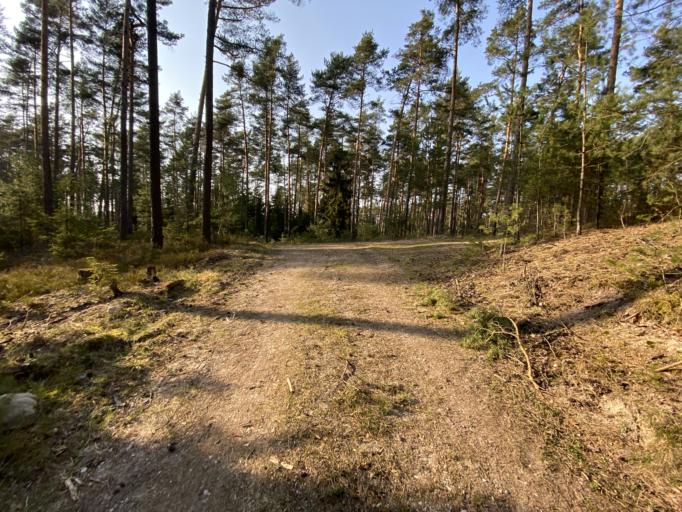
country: DE
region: Bavaria
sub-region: Regierungsbezirk Mittelfranken
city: Buckenhof
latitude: 49.5530
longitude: 11.0673
